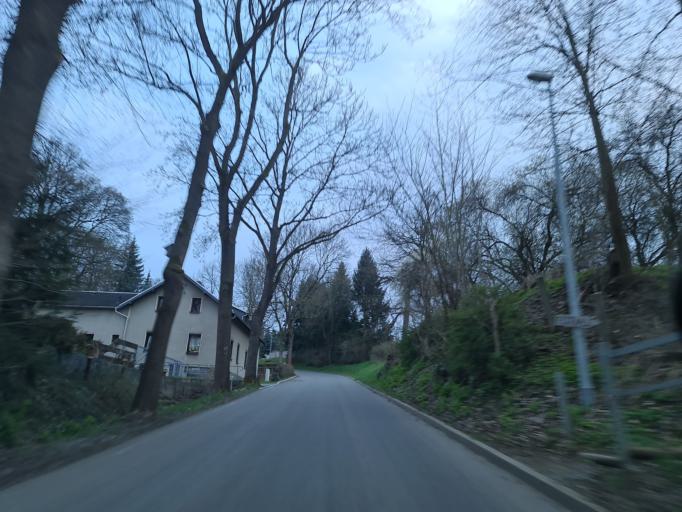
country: DE
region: Saxony
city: Bosenbrunn
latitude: 50.4257
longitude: 12.0920
